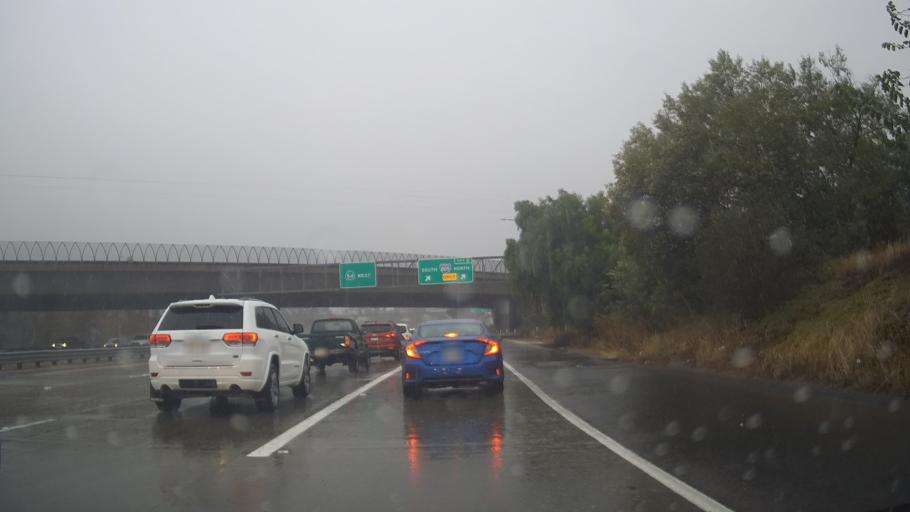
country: US
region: California
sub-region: San Diego County
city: Chula Vista
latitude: 32.6612
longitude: -117.0677
